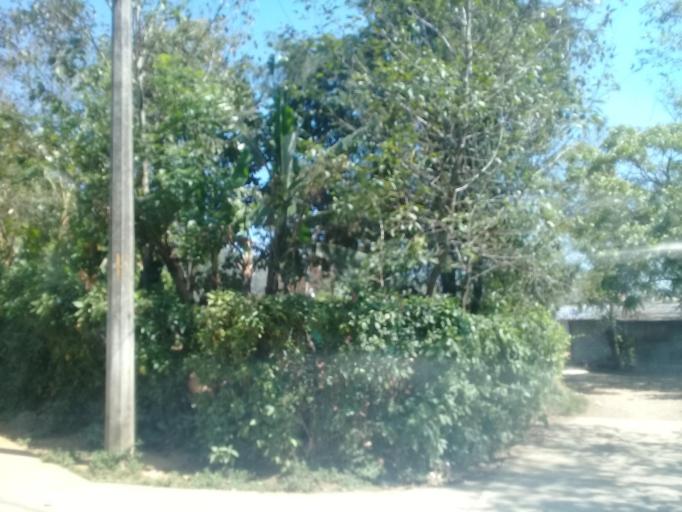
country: MX
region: Veracruz
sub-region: Tlilapan
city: Tonalixco
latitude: 18.7585
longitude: -97.0414
